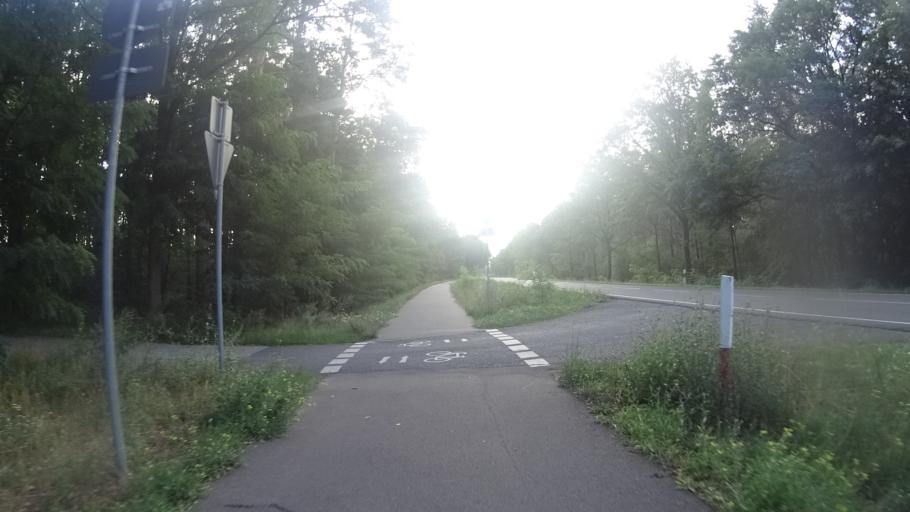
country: DE
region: Brandenburg
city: Premnitz
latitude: 52.5169
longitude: 12.4051
